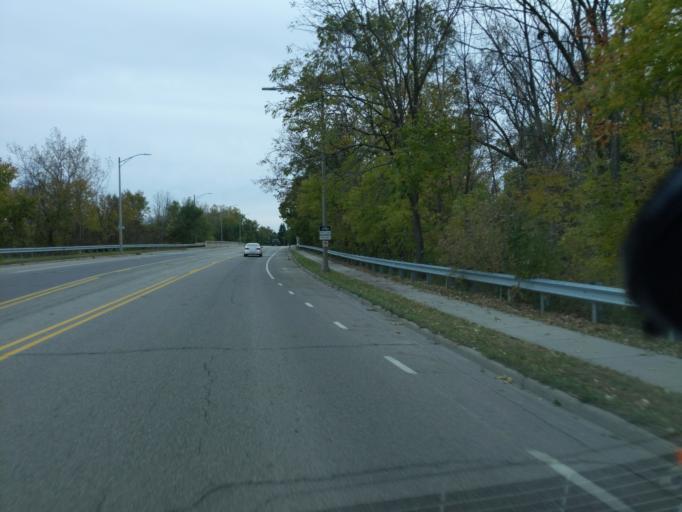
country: US
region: Michigan
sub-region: Ingham County
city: Lansing
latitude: 42.7572
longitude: -84.5674
